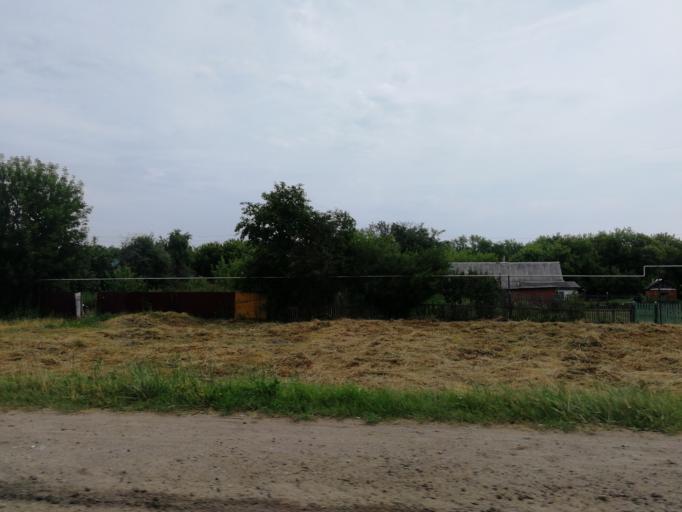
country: RU
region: Tula
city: Tovarkovskiy
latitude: 53.7017
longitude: 38.1606
